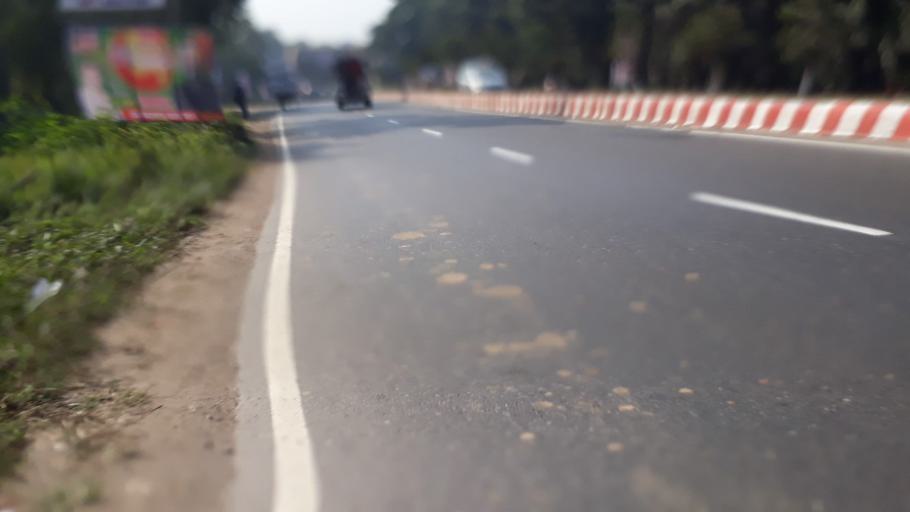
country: BD
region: Dhaka
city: Tungi
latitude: 23.8673
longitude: 90.2715
